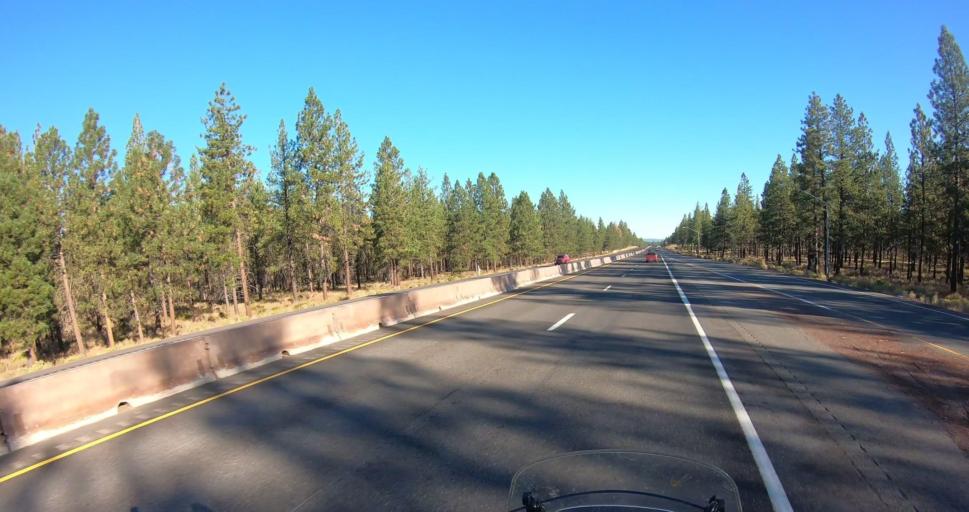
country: US
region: Oregon
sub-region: Deschutes County
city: Deschutes River Woods
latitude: 43.9587
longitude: -121.3482
